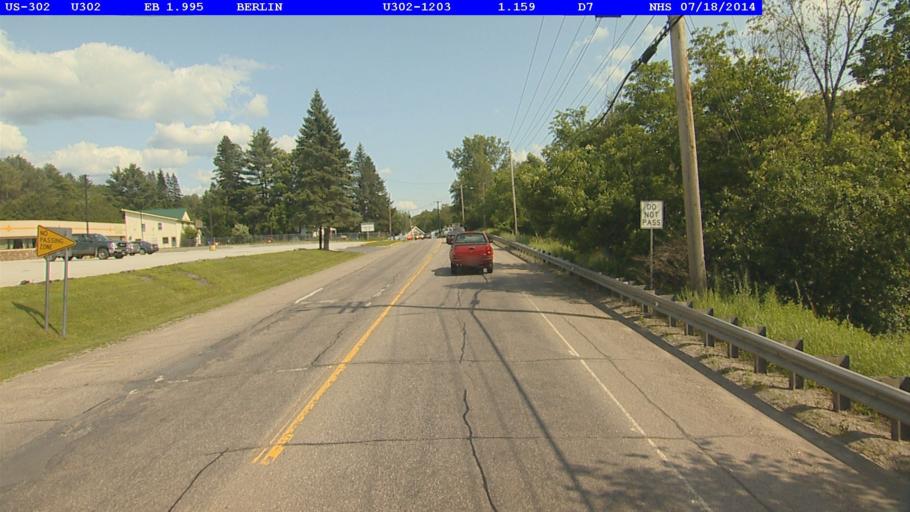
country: US
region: Vermont
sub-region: Washington County
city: Barre
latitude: 44.2206
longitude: -72.5452
